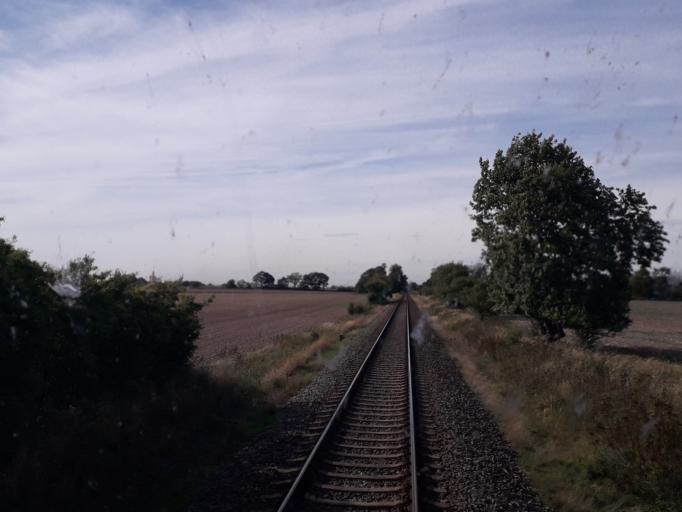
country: DE
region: Brandenburg
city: Neuruppin
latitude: 52.8666
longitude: 12.8768
